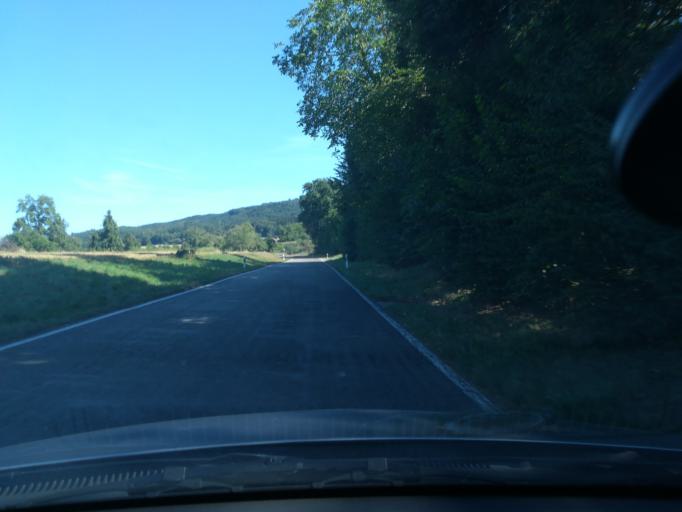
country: DE
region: Baden-Wuerttemberg
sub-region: Freiburg Region
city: Moos
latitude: 47.7146
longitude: 8.8948
